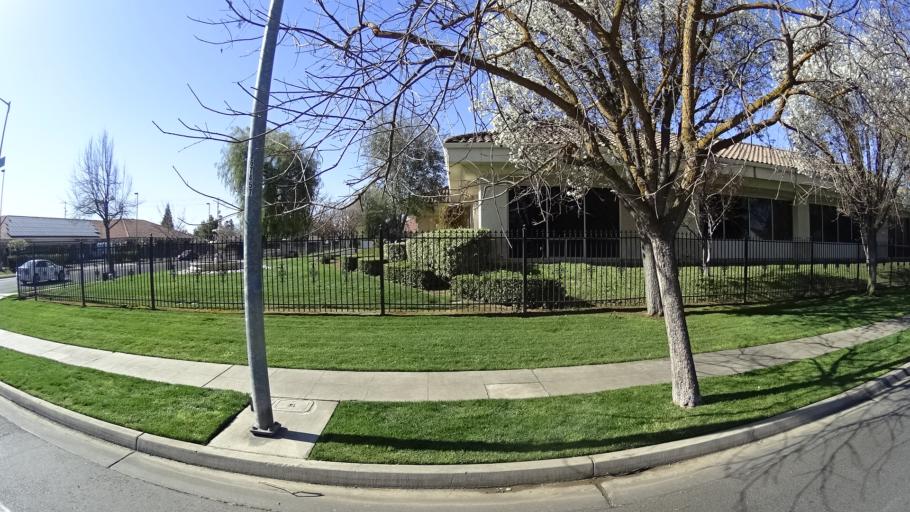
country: US
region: California
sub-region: Fresno County
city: Fresno
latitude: 36.8241
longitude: -119.8521
